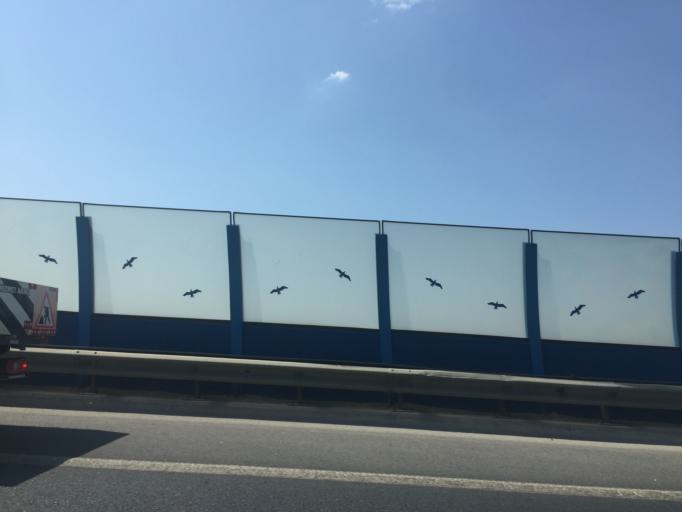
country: TR
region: Izmir
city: Karsiyaka
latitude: 38.4832
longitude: 27.1447
